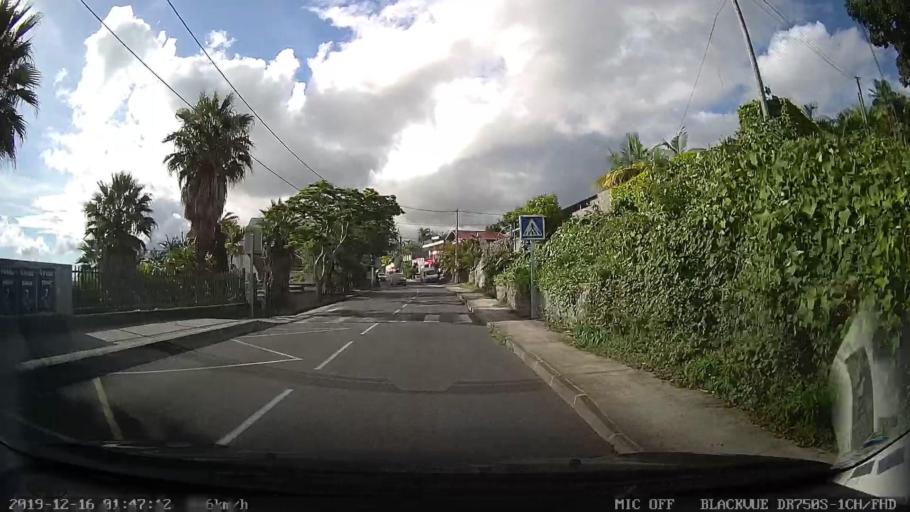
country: RE
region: Reunion
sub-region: Reunion
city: Le Tampon
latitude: -21.2449
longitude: 55.5135
